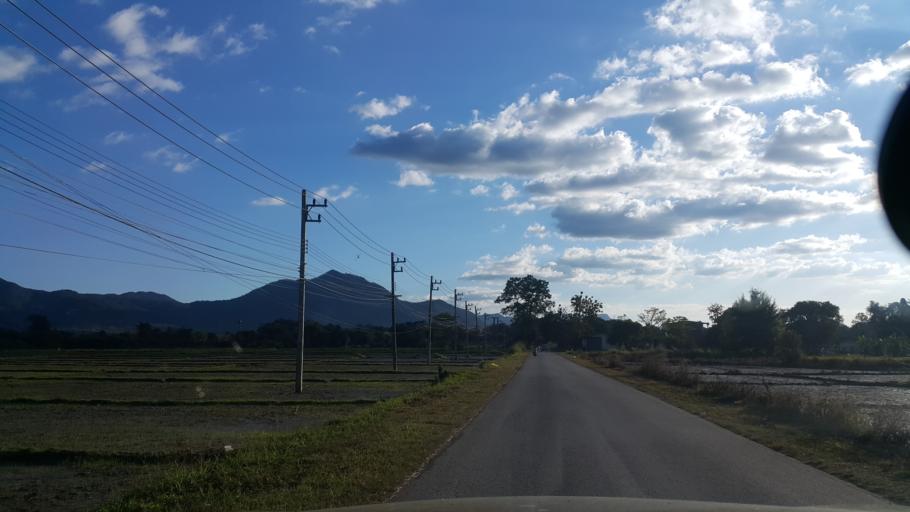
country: TH
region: Chiang Mai
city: Mae On
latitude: 18.7775
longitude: 99.2548
